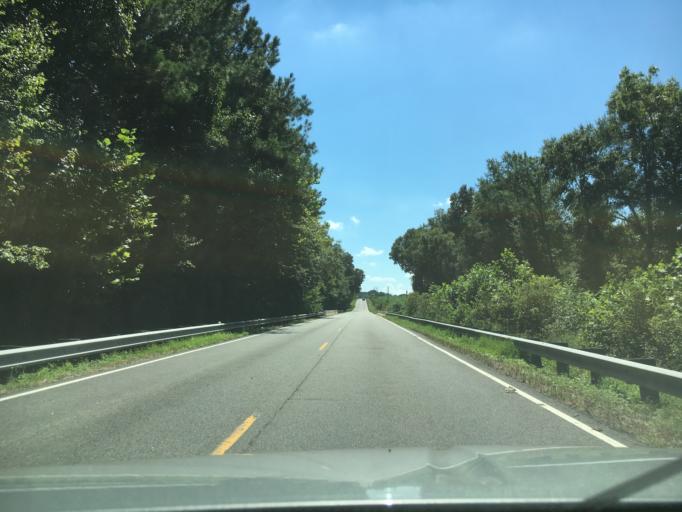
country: US
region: Virginia
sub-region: Amelia County
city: Amelia Court House
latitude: 37.4046
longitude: -77.8952
